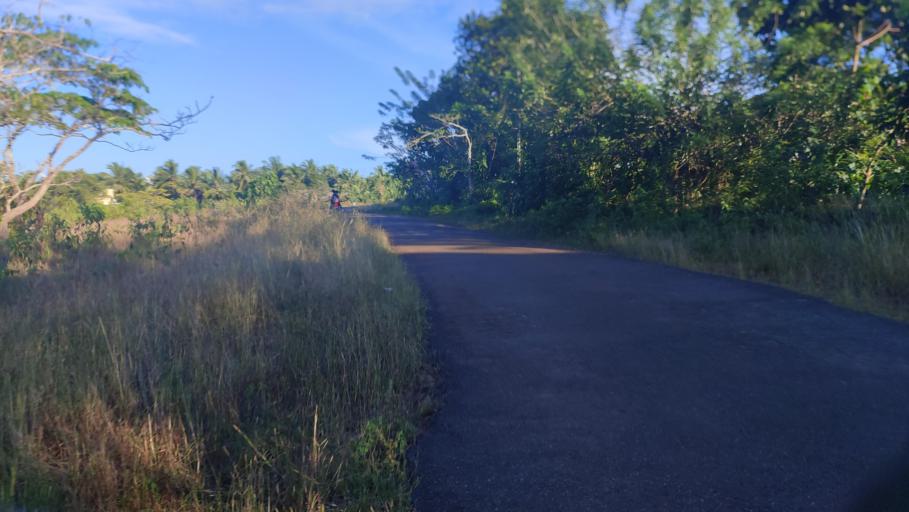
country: IN
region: Kerala
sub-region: Kasaragod District
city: Kasaragod
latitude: 12.4997
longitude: 75.0804
